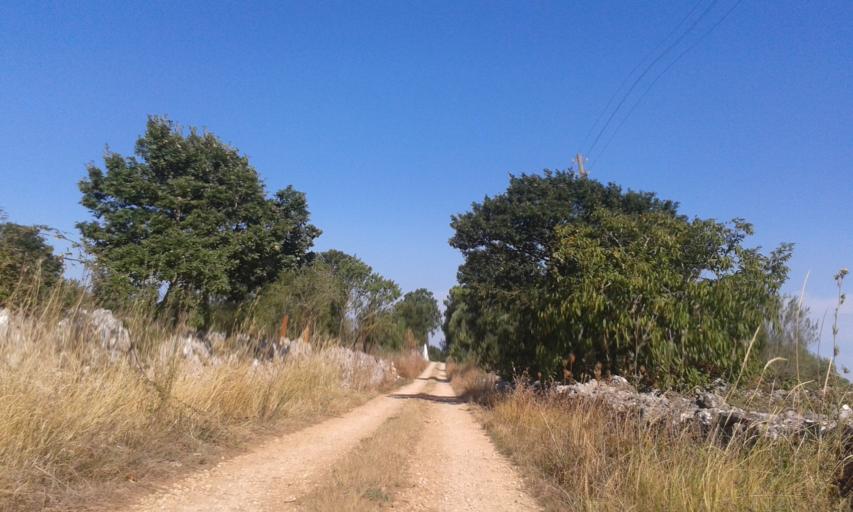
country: IT
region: Apulia
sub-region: Provincia di Bari
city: Gioia del Colle
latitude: 40.7750
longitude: 16.9691
